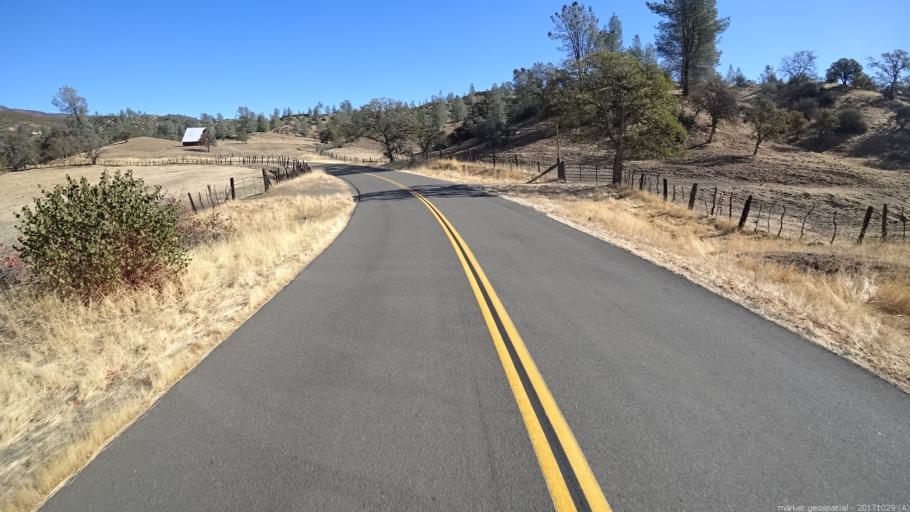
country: US
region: California
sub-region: Trinity County
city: Lewiston
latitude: 40.4145
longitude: -122.7700
